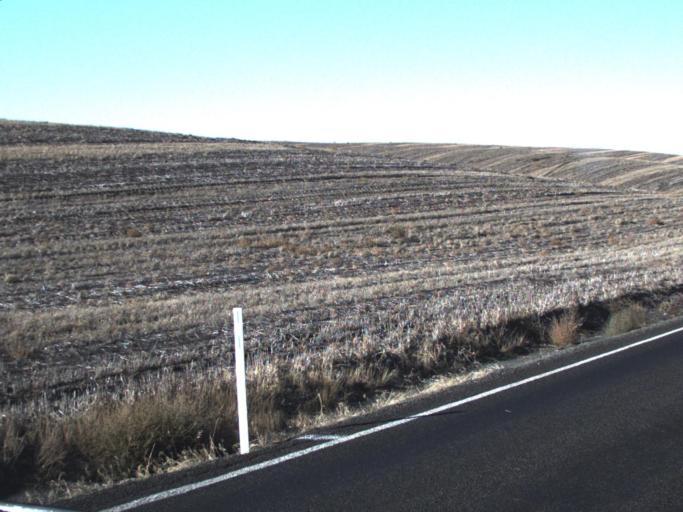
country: US
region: Washington
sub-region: Walla Walla County
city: Walla Walla
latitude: 46.1205
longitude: -118.3722
